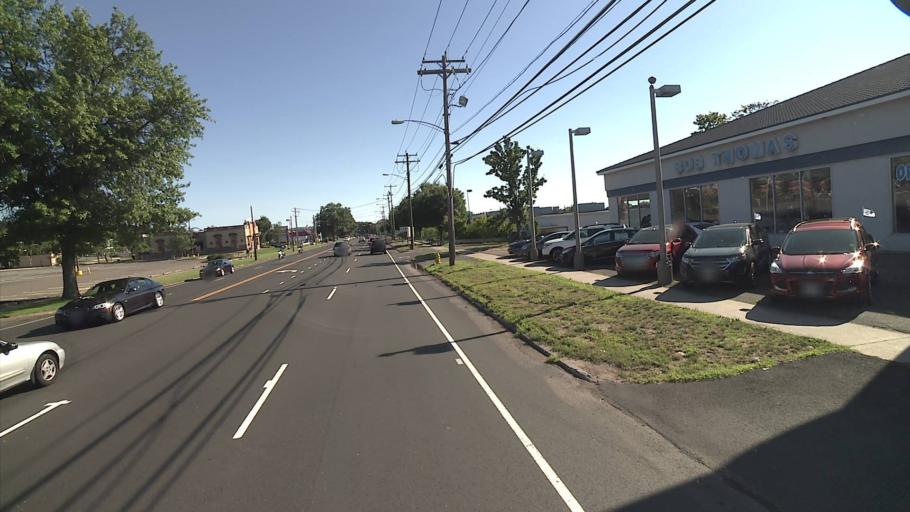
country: US
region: Connecticut
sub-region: New Haven County
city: Hamden
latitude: 41.3712
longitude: -72.9180
